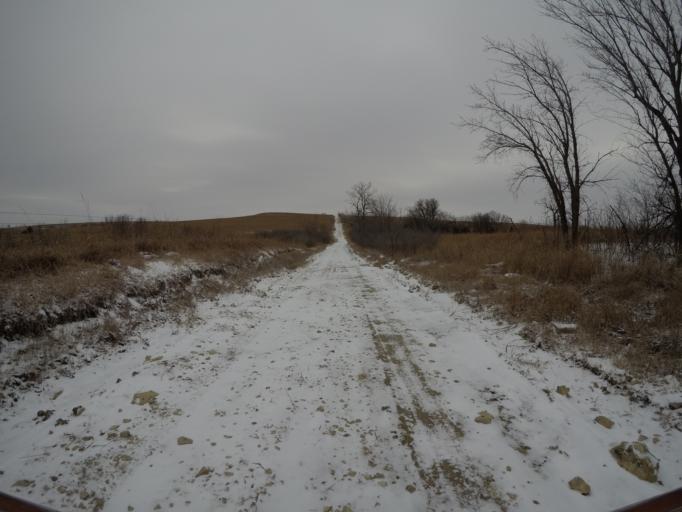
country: US
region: Kansas
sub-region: Wabaunsee County
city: Alma
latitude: 38.8804
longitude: -96.1136
